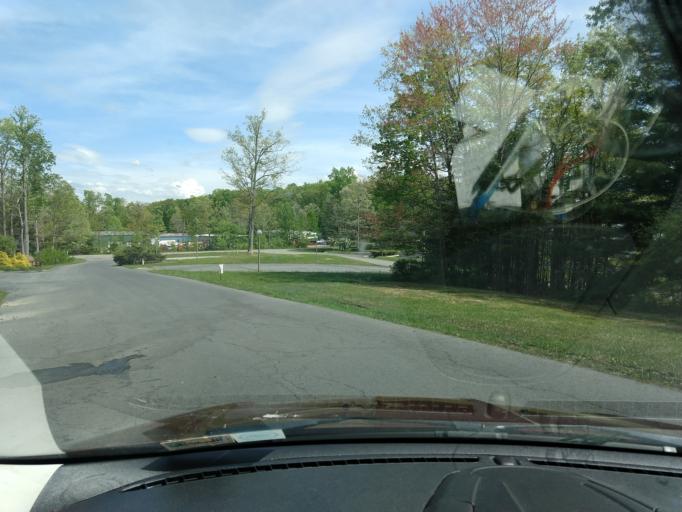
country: US
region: West Virginia
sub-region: Raleigh County
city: Stanaford
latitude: 37.7932
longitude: -81.1187
